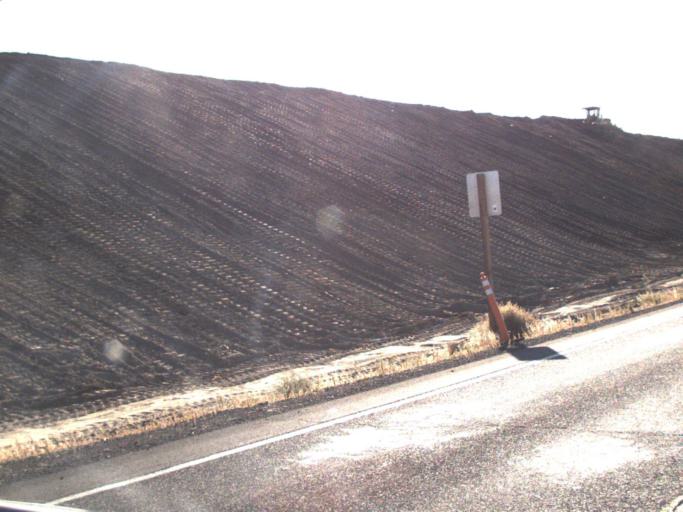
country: US
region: Washington
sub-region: Walla Walla County
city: Burbank
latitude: 46.2148
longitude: -118.9046
